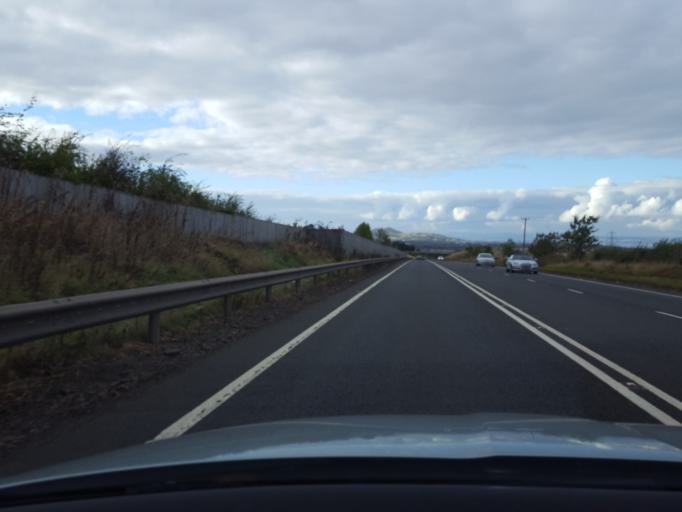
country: GB
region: Scotland
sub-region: Midlothian
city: Dalkeith
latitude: 55.8990
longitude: -3.0175
